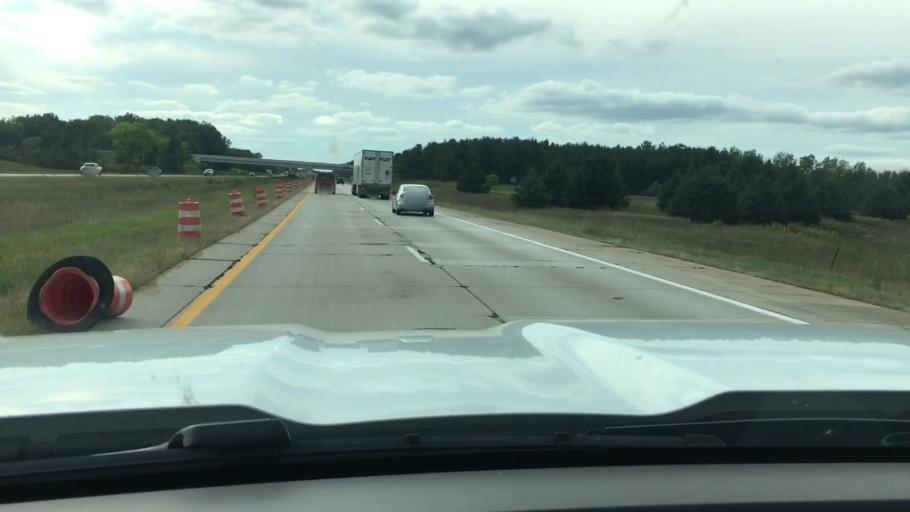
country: US
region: Michigan
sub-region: Lapeer County
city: Imlay City
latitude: 43.0083
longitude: -83.1593
